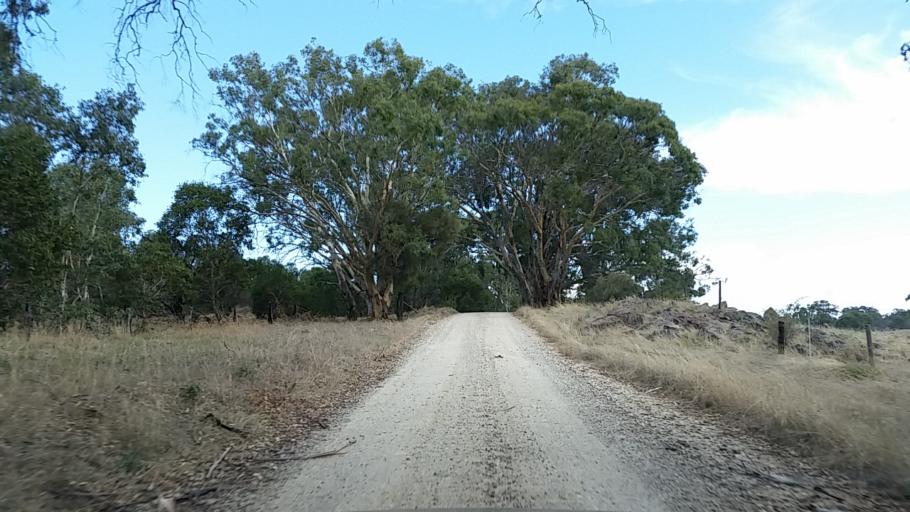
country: AU
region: South Australia
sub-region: Barossa
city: Angaston
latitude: -34.5662
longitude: 139.0743
